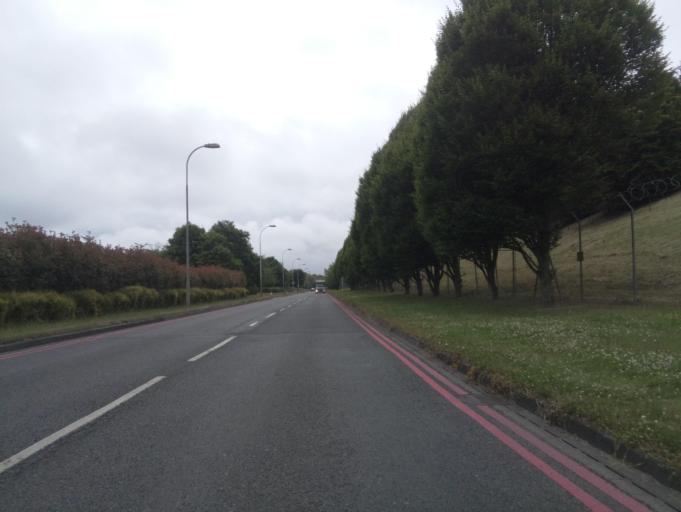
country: GB
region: England
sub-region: Surrey
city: Horley
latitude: 51.1638
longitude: -0.1839
